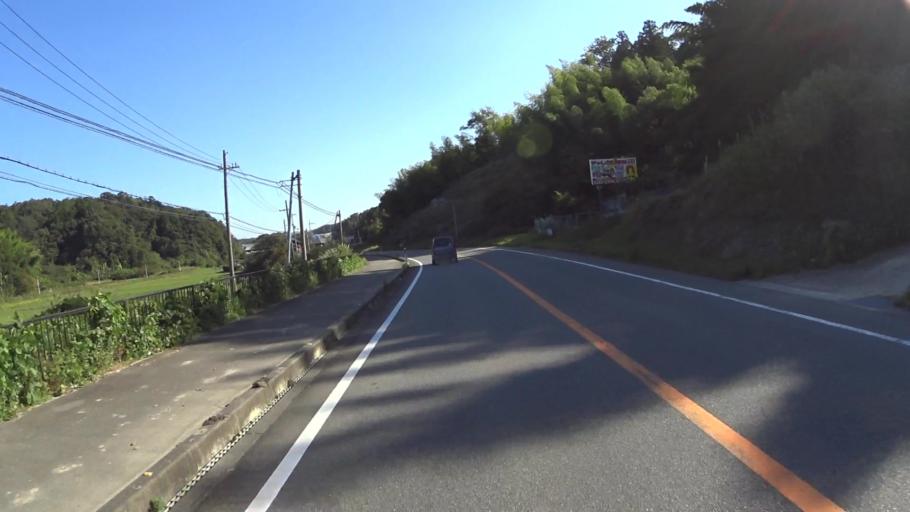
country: JP
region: Kyoto
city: Miyazu
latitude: 35.6431
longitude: 135.0512
